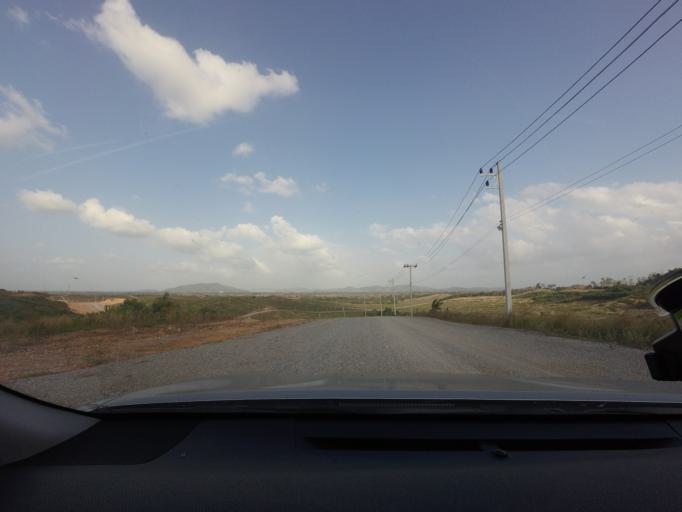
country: TH
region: Pattani
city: Mae Lan
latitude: 6.6046
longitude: 101.2487
